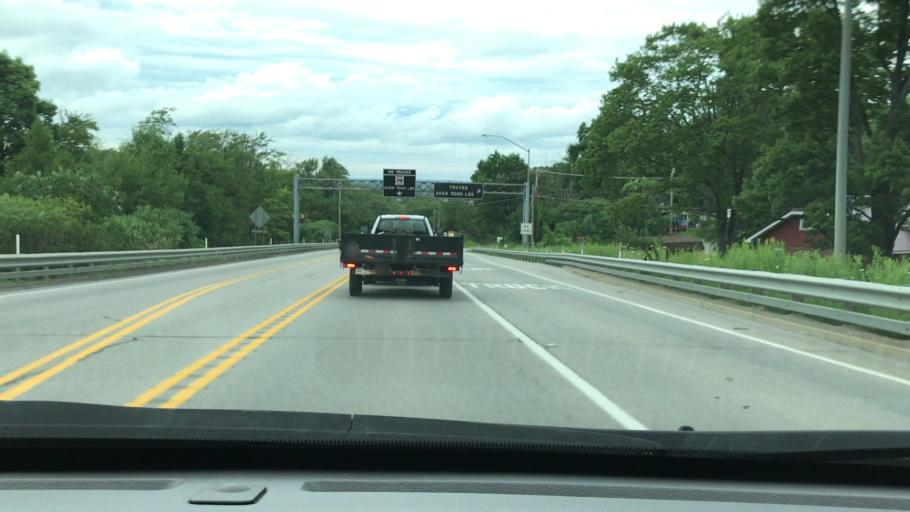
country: US
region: Pennsylvania
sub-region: Elk County
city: Ridgway
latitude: 41.4108
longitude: -78.7116
